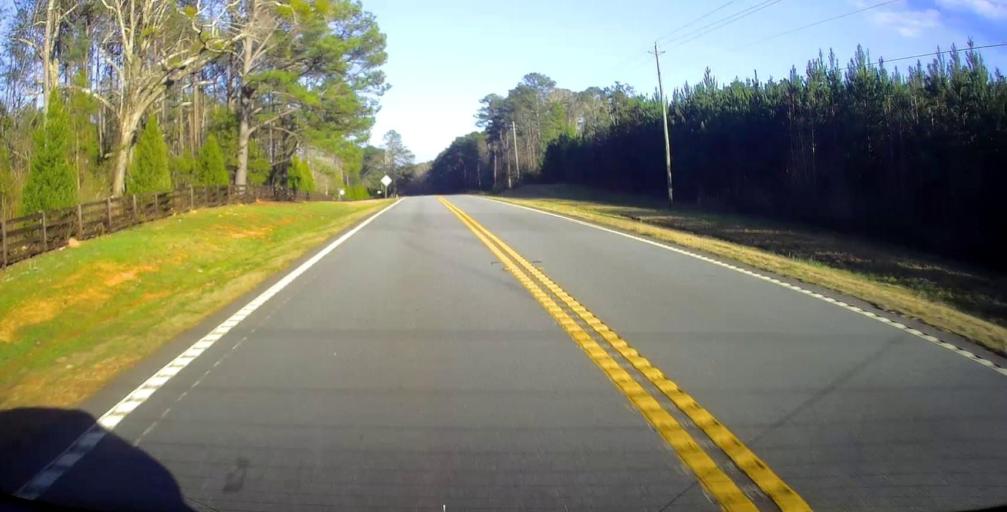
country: US
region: Alabama
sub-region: Chambers County
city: Valley
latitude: 32.7434
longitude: -85.0493
